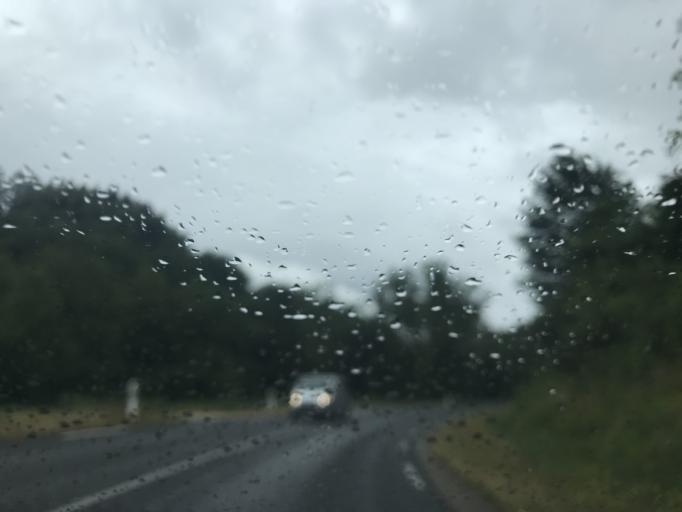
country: FR
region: Auvergne
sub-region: Departement du Puy-de-Dome
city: Job
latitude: 45.6209
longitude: 3.7225
